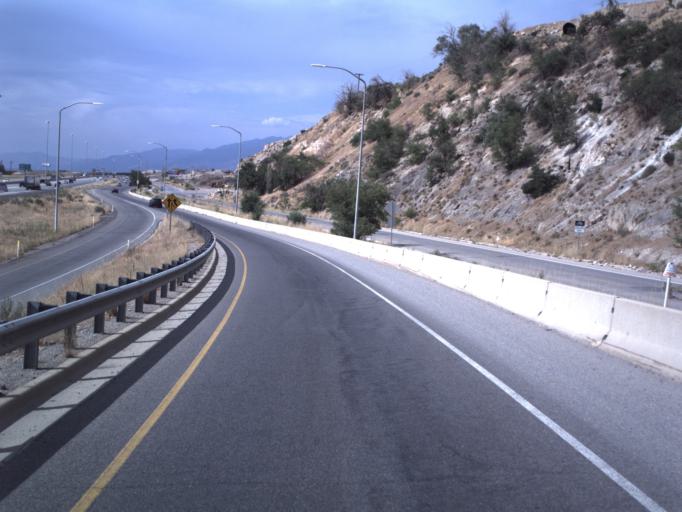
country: US
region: Utah
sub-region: Davis County
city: North Salt Lake
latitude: 40.8190
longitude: -111.9159
